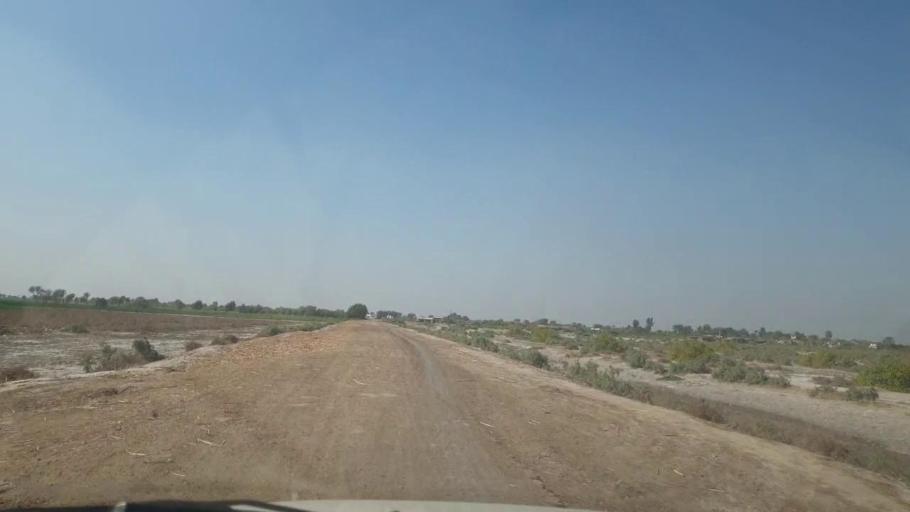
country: PK
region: Sindh
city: Mirpur Khas
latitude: 25.4760
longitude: 69.1208
